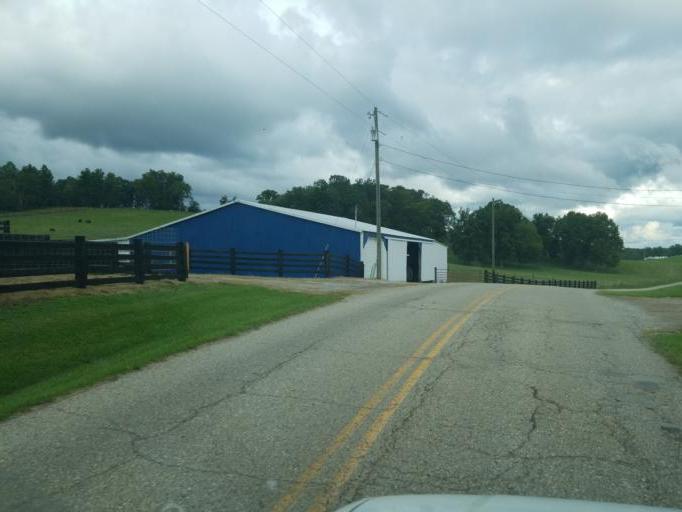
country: US
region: Ohio
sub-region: Jackson County
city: Oak Hill
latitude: 38.9397
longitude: -82.5872
